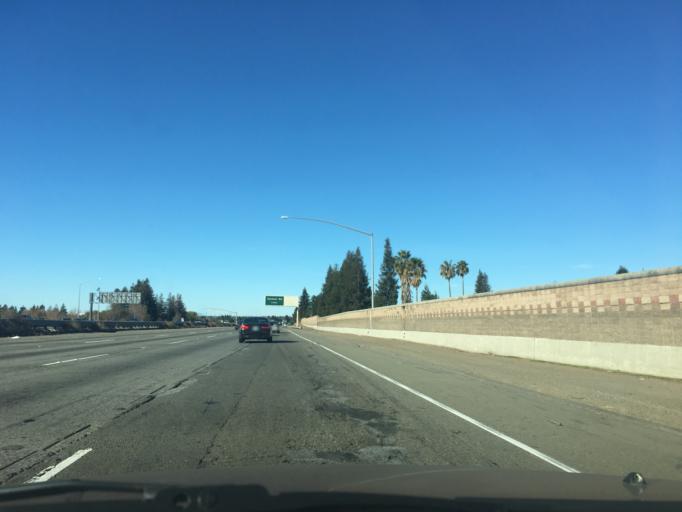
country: US
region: California
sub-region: Santa Clara County
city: Milpitas
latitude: 37.4987
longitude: -121.9263
